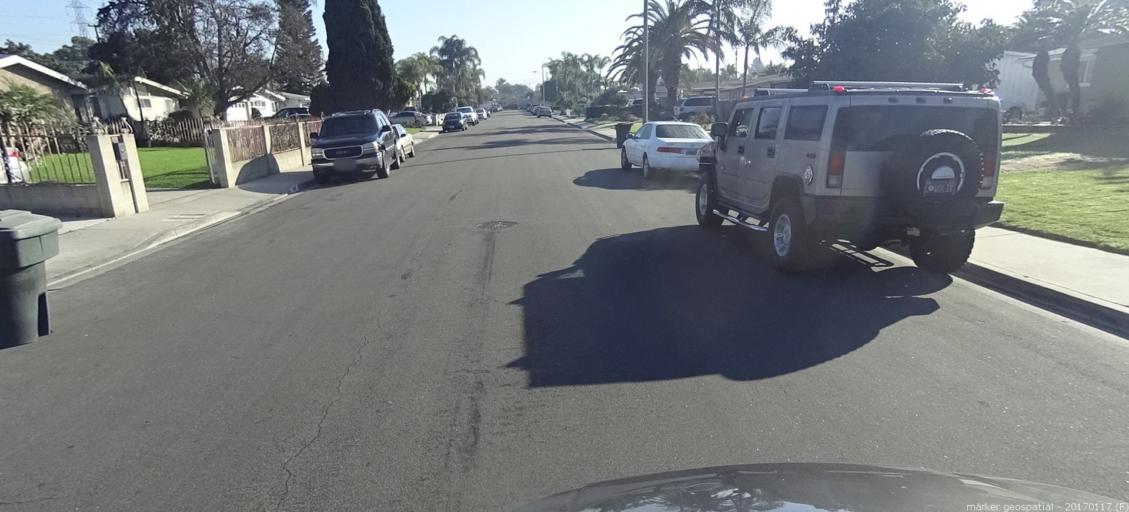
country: US
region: California
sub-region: Orange County
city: Stanton
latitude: 33.8055
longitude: -117.9663
